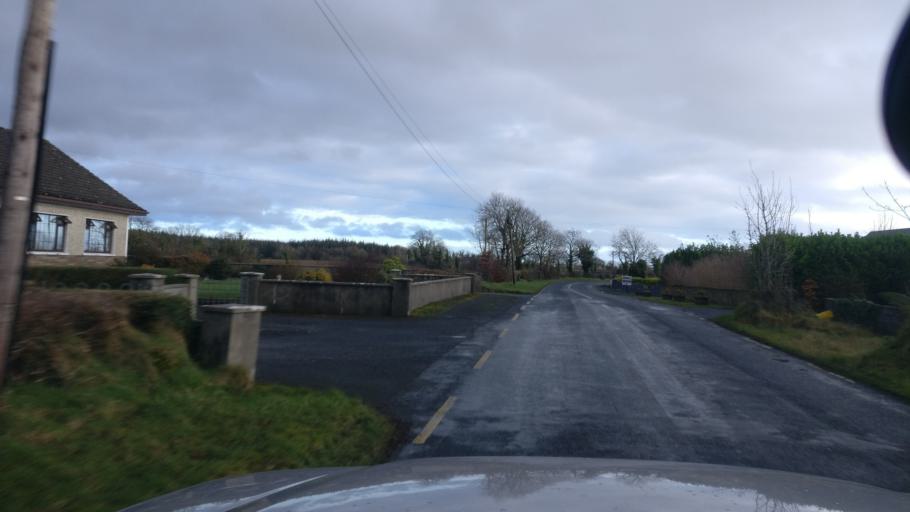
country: IE
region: Connaught
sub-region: County Galway
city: Athenry
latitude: 53.2951
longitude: -8.6513
